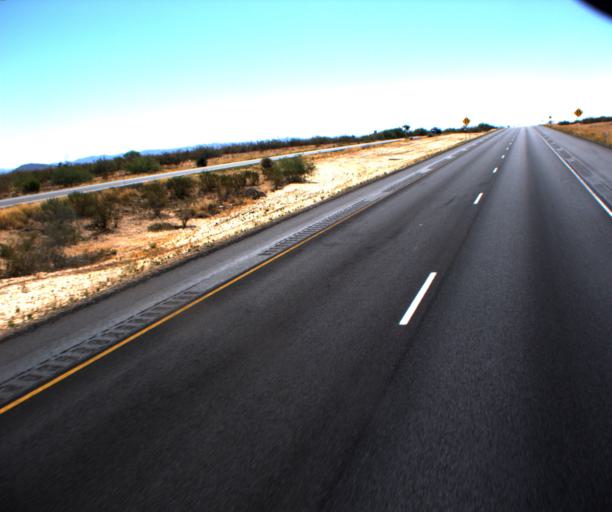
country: US
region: Arizona
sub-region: Yavapai County
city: Congress
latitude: 34.0592
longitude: -112.8589
